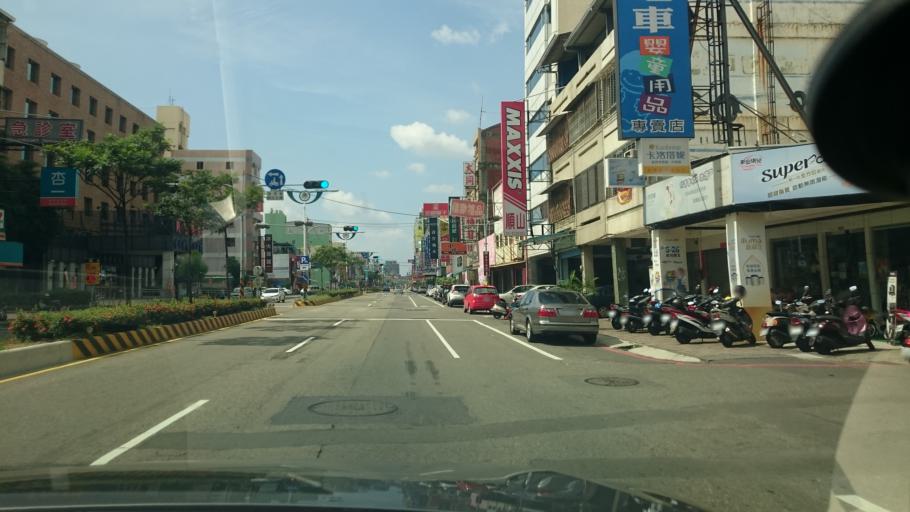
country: TW
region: Taiwan
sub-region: Nantou
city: Nantou
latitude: 23.9585
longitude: 120.5667
